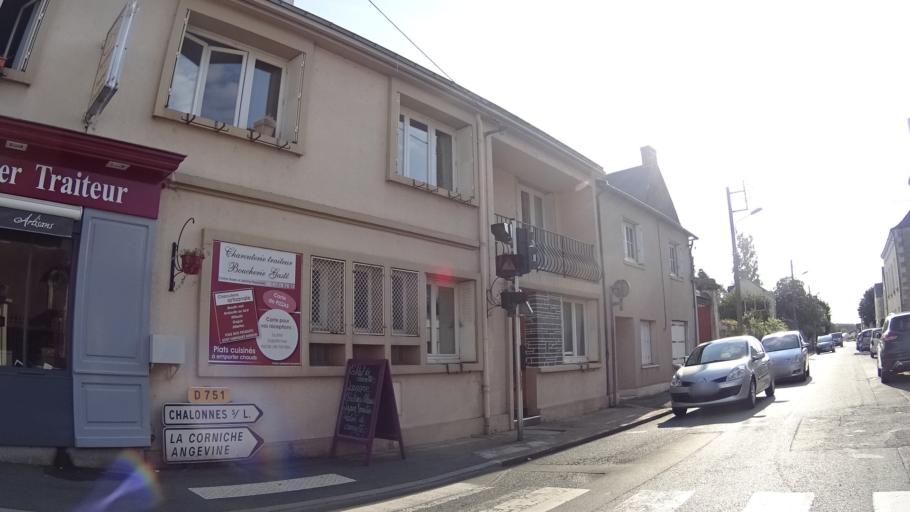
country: FR
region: Pays de la Loire
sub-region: Departement de Maine-et-Loire
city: Rochefort-sur-Loire
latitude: 47.3573
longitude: -0.6558
